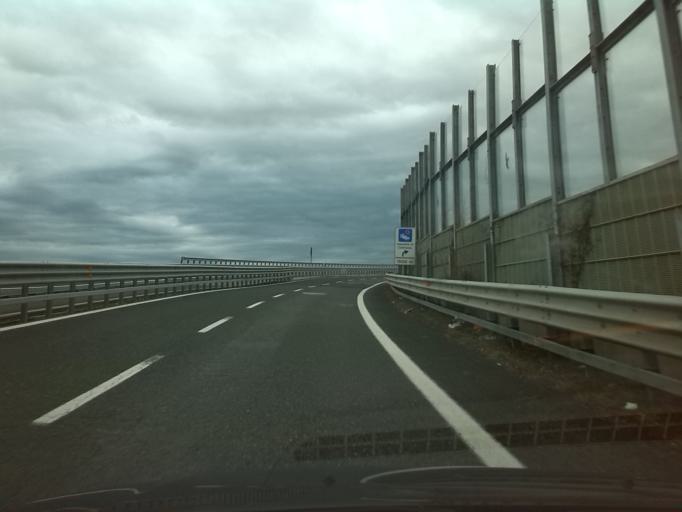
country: IT
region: Friuli Venezia Giulia
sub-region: Provincia di Trieste
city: Domio
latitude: 45.6300
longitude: 13.8209
